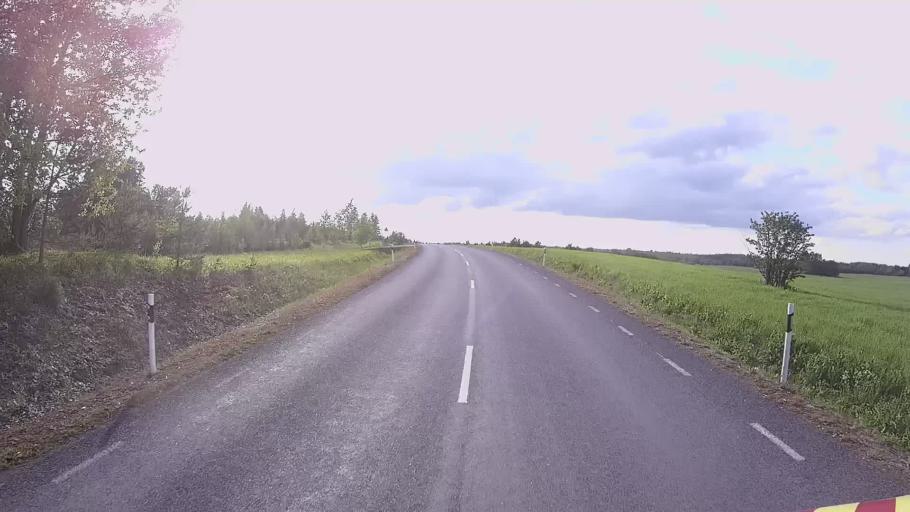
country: EE
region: Jogevamaa
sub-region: Mustvee linn
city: Mustvee
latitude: 59.0440
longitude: 27.0552
